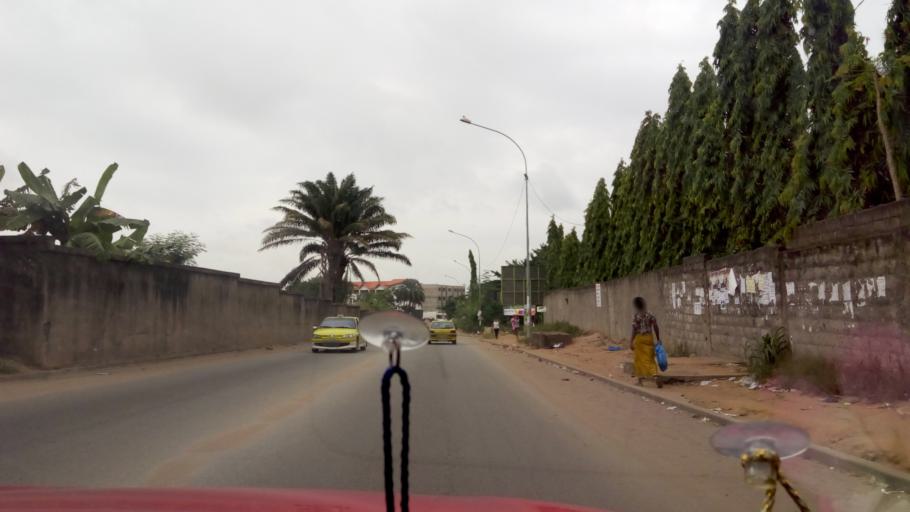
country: CI
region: Lagunes
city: Abidjan
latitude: 5.3446
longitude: -3.9747
